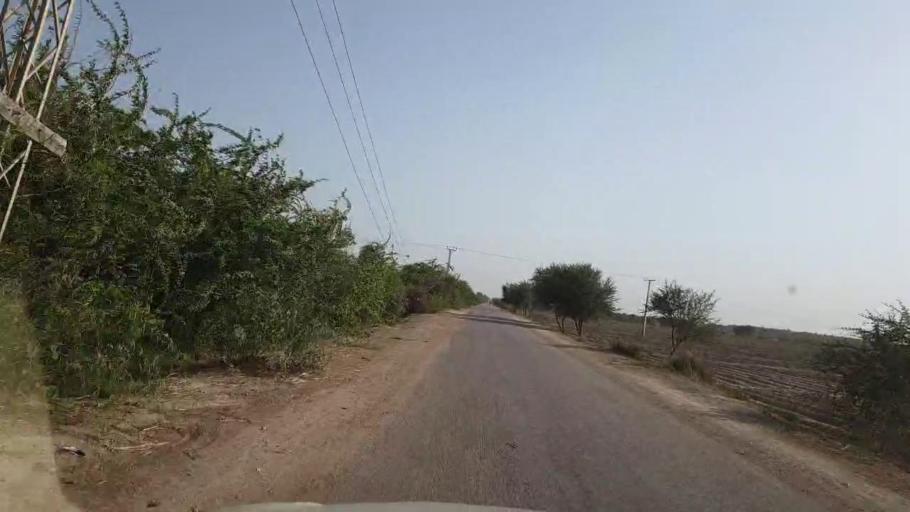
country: PK
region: Sindh
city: Tando Ghulam Ali
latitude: 25.1035
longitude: 68.8690
